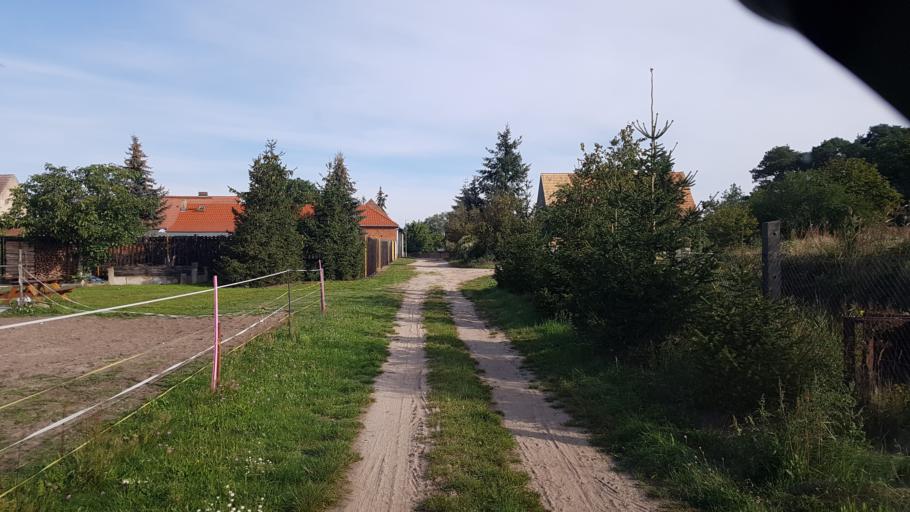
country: DE
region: Brandenburg
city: Finsterwalde
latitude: 51.6622
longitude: 13.6815
